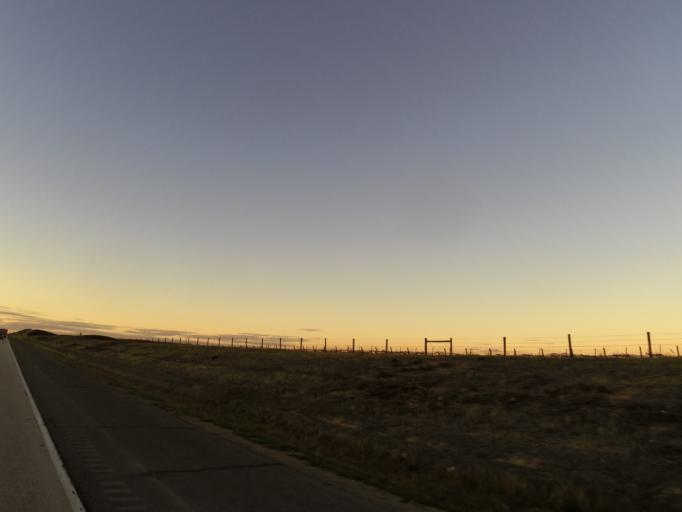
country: US
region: California
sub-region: Monterey County
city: King City
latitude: 36.0203
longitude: -120.9287
